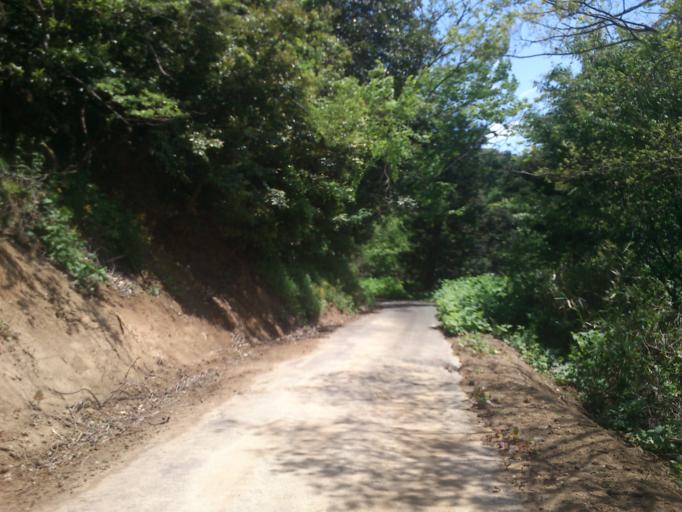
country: JP
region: Kyoto
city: Miyazu
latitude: 35.7165
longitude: 135.1360
